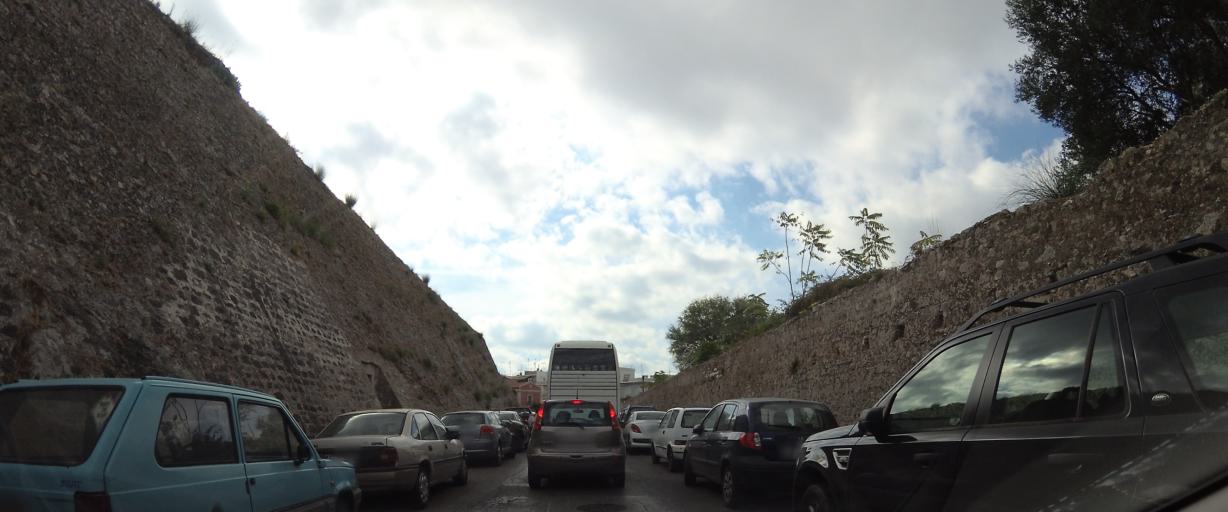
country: GR
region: Ionian Islands
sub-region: Nomos Kerkyras
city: Kerkyra
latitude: 39.6247
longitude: 19.9157
